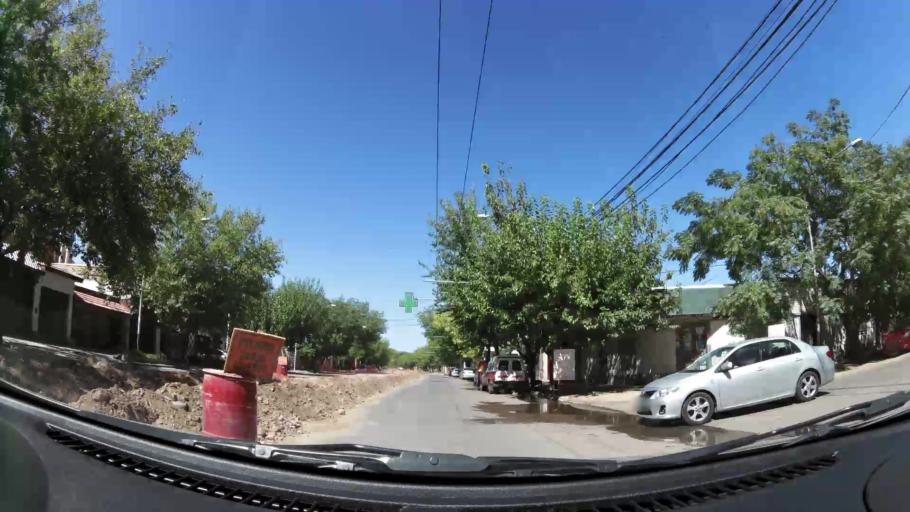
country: AR
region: Mendoza
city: Mendoza
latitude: -32.8914
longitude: -68.8062
